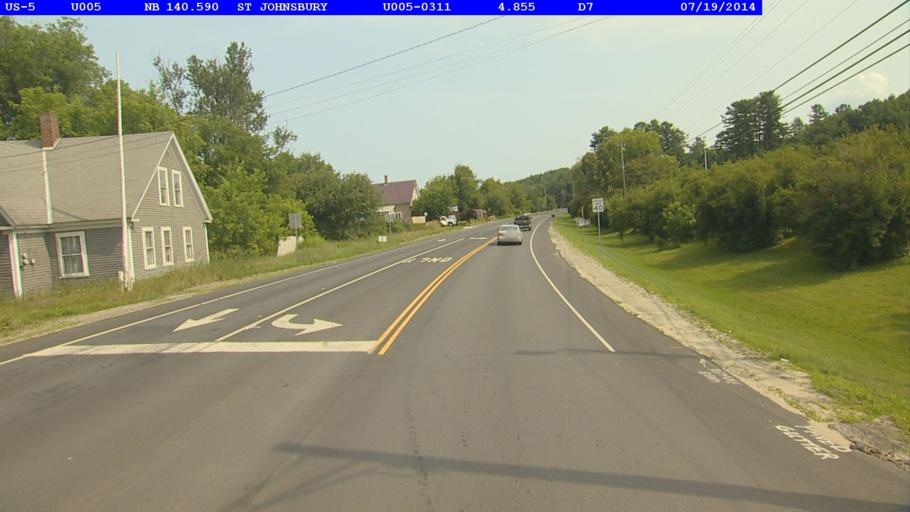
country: US
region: Vermont
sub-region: Caledonia County
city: St Johnsbury
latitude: 44.4611
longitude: -72.0154
